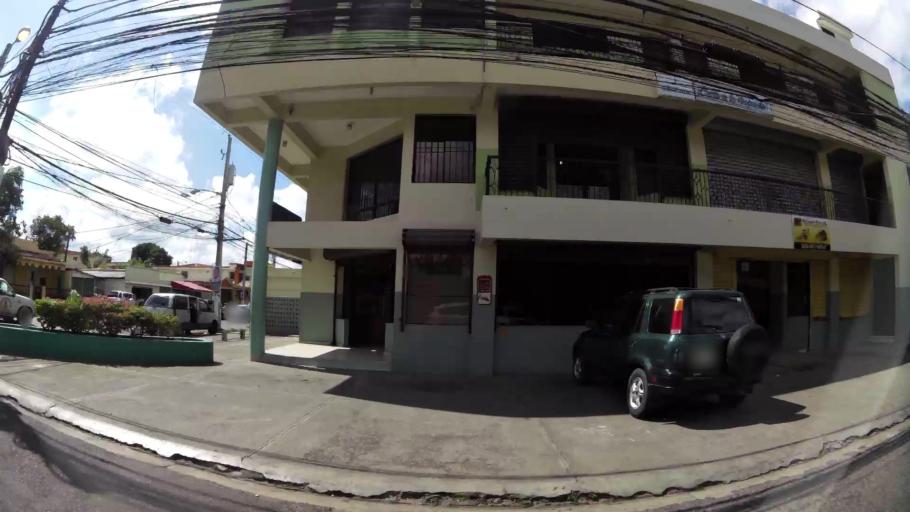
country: DO
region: Santiago
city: Santiago de los Caballeros
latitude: 19.4706
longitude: -70.6920
